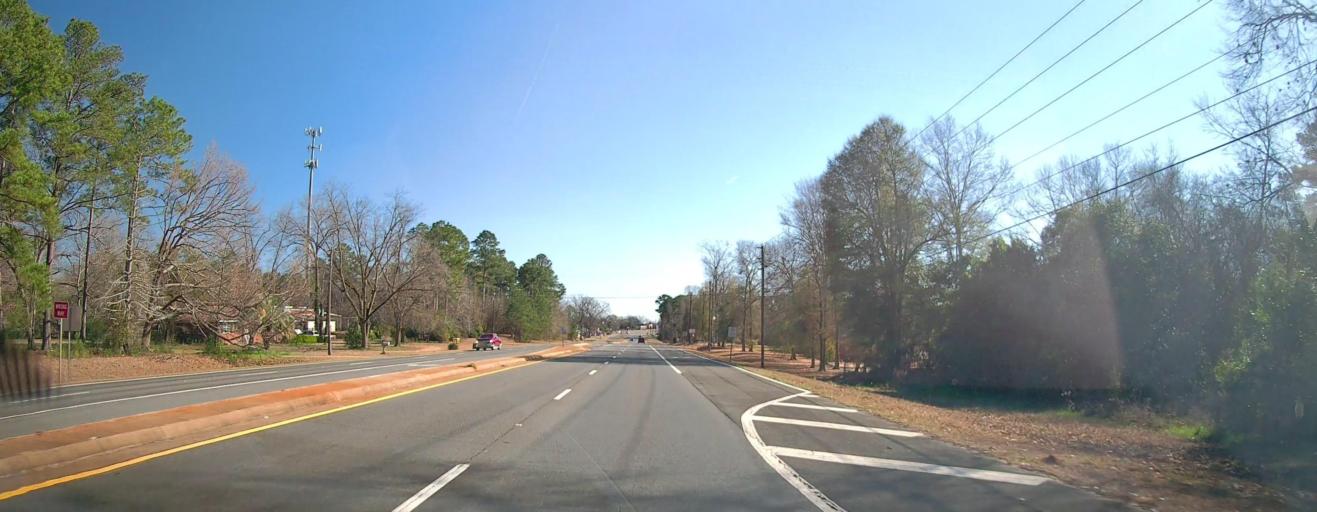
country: US
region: Georgia
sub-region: Sumter County
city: Americus
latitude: 32.0964
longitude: -84.2425
